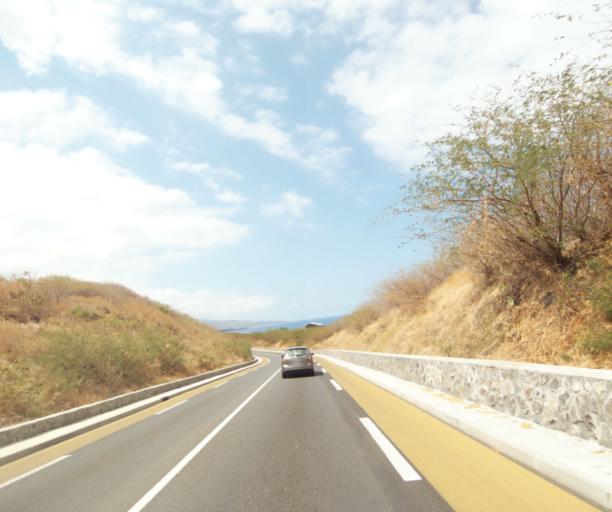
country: RE
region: Reunion
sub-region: Reunion
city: Trois-Bassins
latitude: -21.0962
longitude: 55.2463
